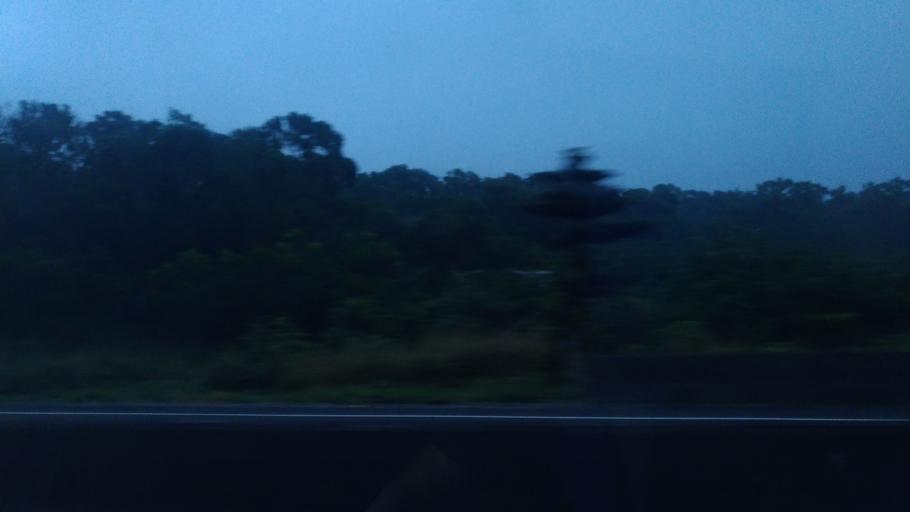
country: TW
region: Taiwan
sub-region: Miaoli
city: Miaoli
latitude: 24.5815
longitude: 120.7219
